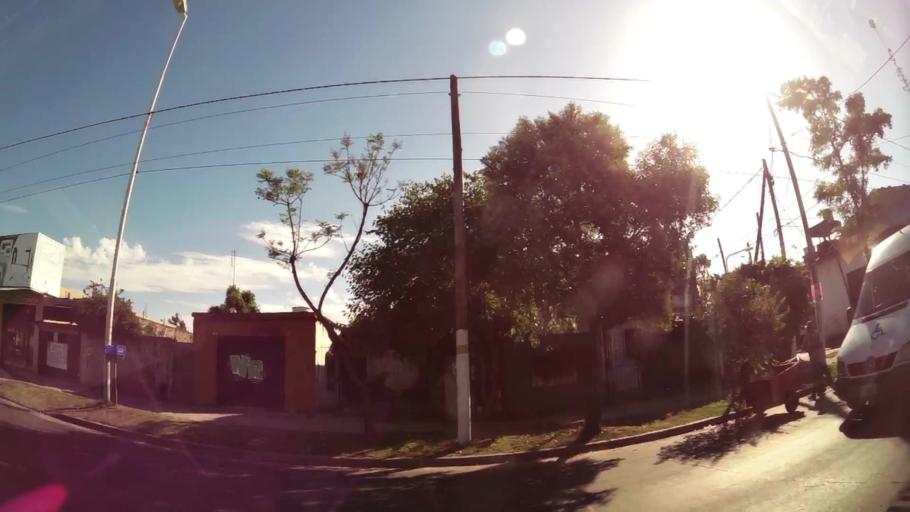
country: AR
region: Buenos Aires
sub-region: Partido de Tigre
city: Tigre
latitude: -34.4854
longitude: -58.6655
